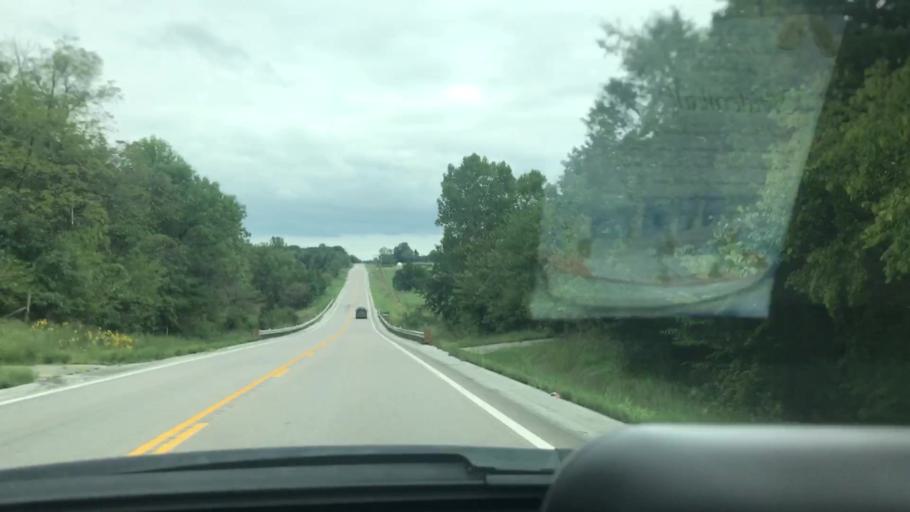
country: US
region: Missouri
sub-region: Dallas County
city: Buffalo
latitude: 37.7167
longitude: -93.1193
